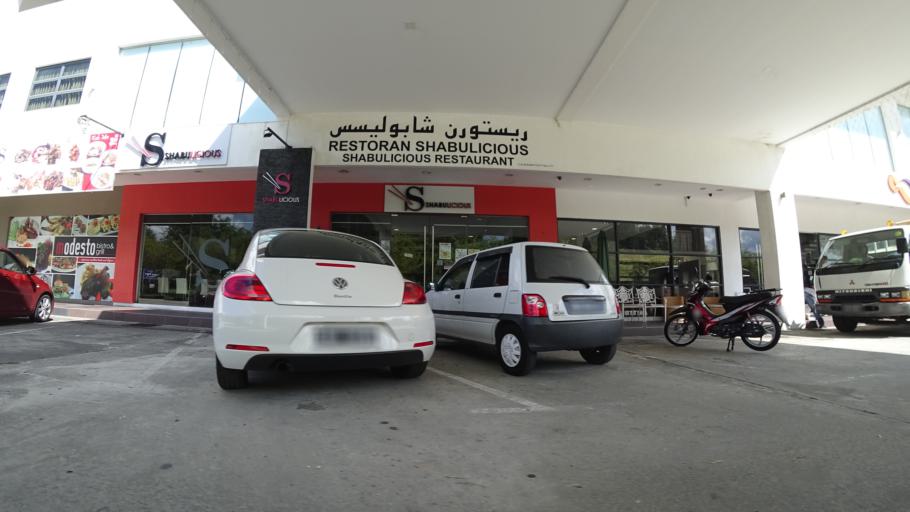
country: BN
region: Brunei and Muara
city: Bandar Seri Begawan
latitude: 4.9162
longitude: 114.9124
